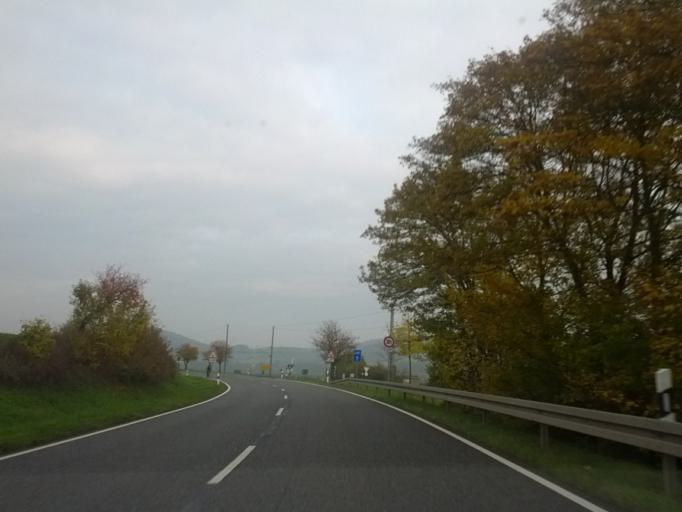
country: DE
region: Hesse
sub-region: Regierungsbezirk Kassel
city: Herleshausen
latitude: 51.0026
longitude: 10.1842
